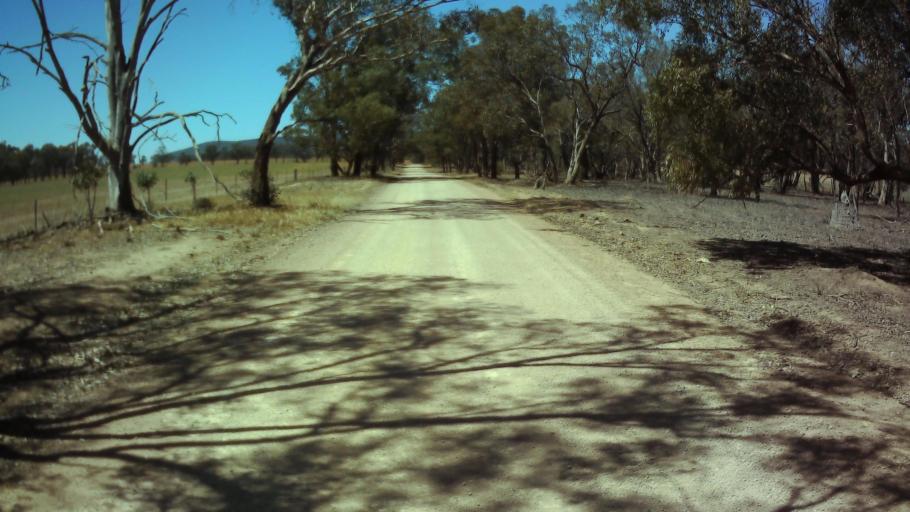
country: AU
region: New South Wales
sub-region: Weddin
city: Grenfell
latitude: -33.9250
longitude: 148.0783
